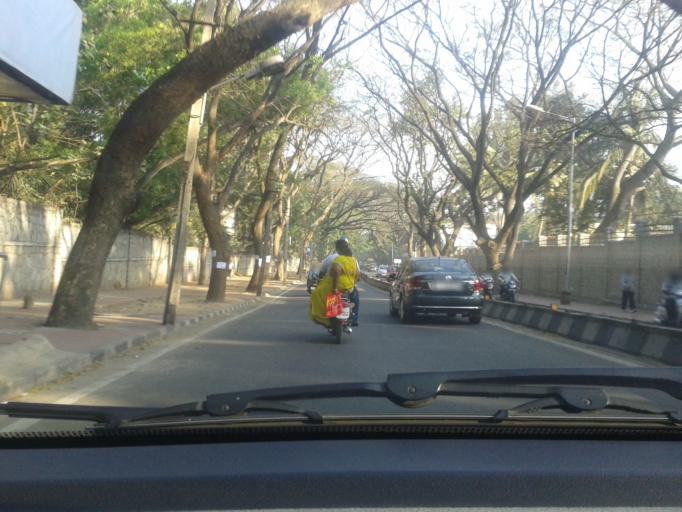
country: IN
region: Karnataka
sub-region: Bangalore Urban
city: Bangalore
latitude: 13.0161
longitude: 77.5727
